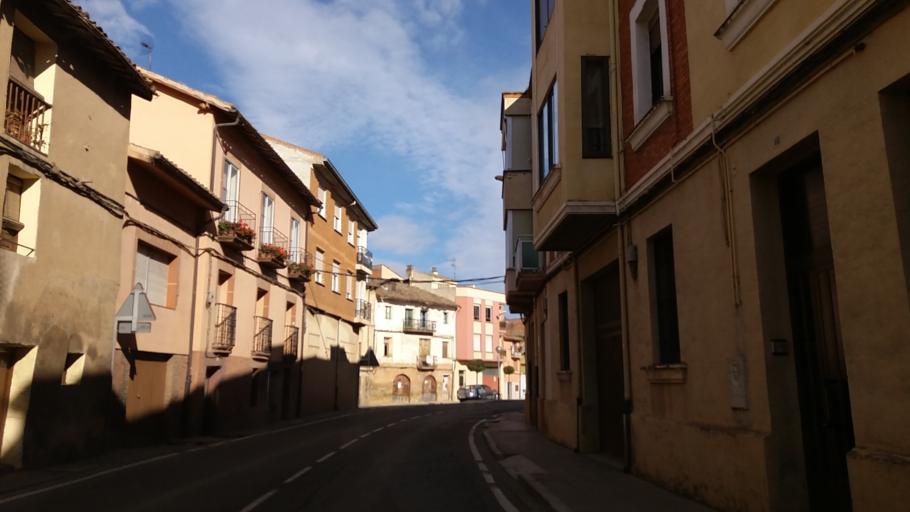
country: ES
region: La Rioja
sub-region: Provincia de La Rioja
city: Fuenmayor
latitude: 42.4678
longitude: -2.5613
